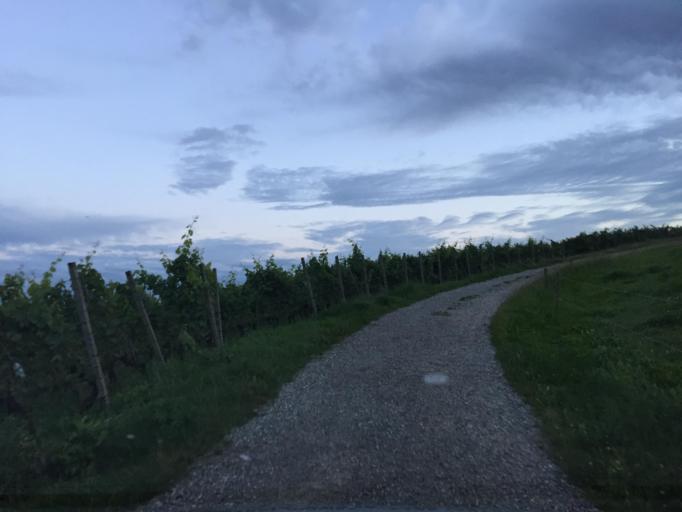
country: CH
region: Schaffhausen
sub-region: Bezirk Unterklettgau
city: Wilchingen
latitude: 47.6664
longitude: 8.4276
